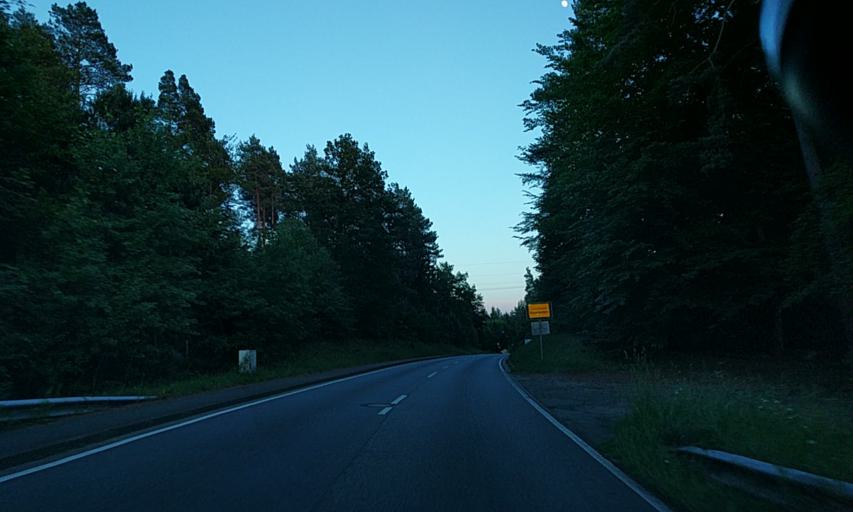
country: DE
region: Rheinland-Pfalz
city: Otterbach
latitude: 49.4647
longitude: 7.7210
